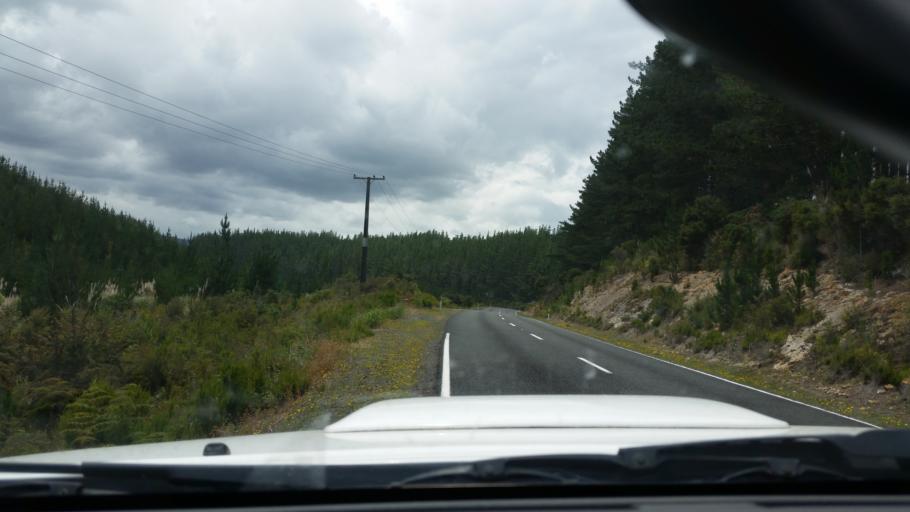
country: NZ
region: Northland
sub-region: Kaipara District
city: Dargaville
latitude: -35.8226
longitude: 173.7042
